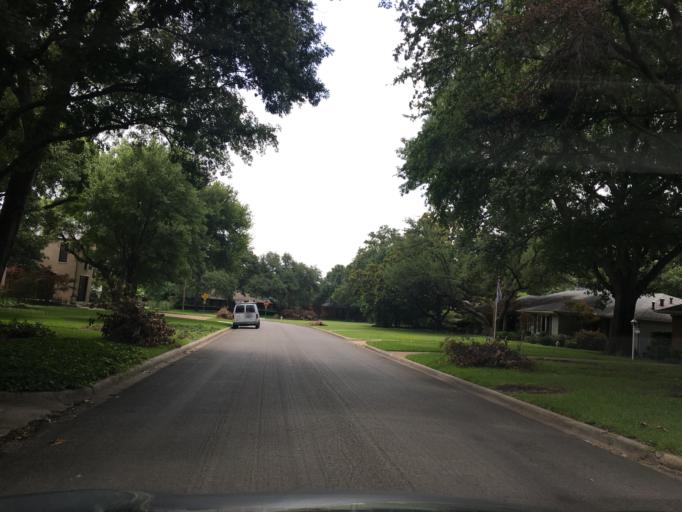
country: US
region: Texas
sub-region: Dallas County
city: University Park
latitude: 32.9028
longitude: -96.7978
